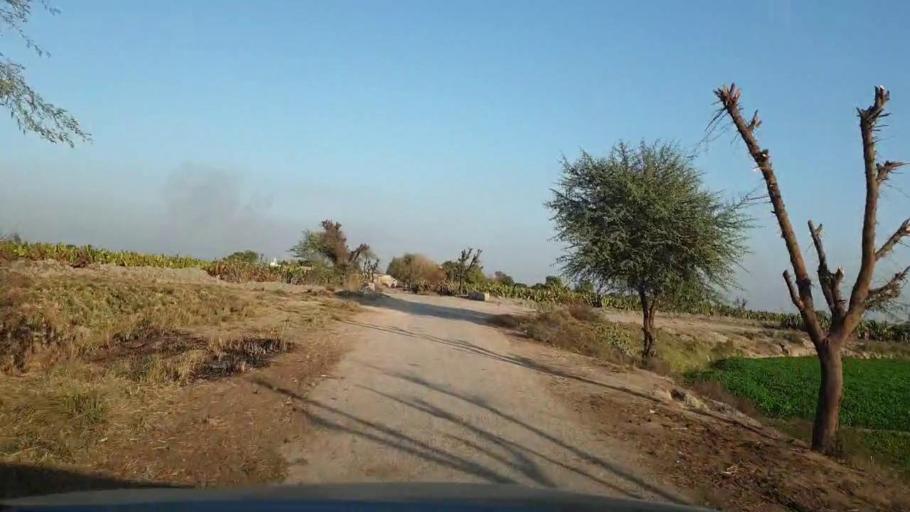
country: PK
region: Sindh
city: Matiari
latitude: 25.6168
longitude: 68.5979
